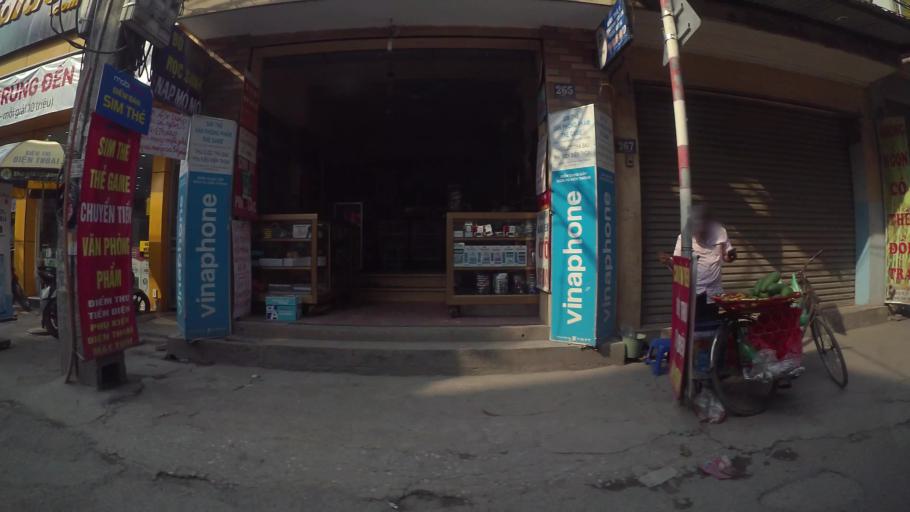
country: VN
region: Ha Noi
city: Thanh Xuan
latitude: 20.9844
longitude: 105.8236
